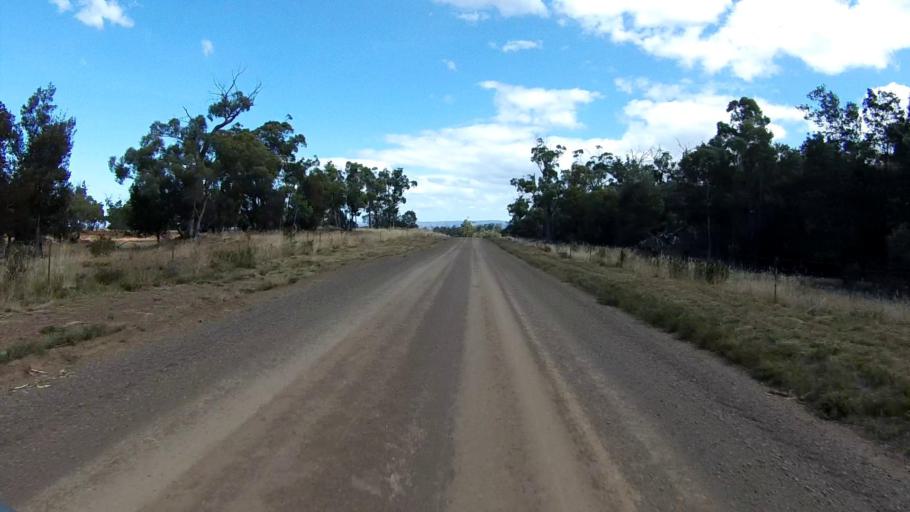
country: AU
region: Tasmania
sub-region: Break O'Day
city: St Helens
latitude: -41.9802
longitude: 148.0671
